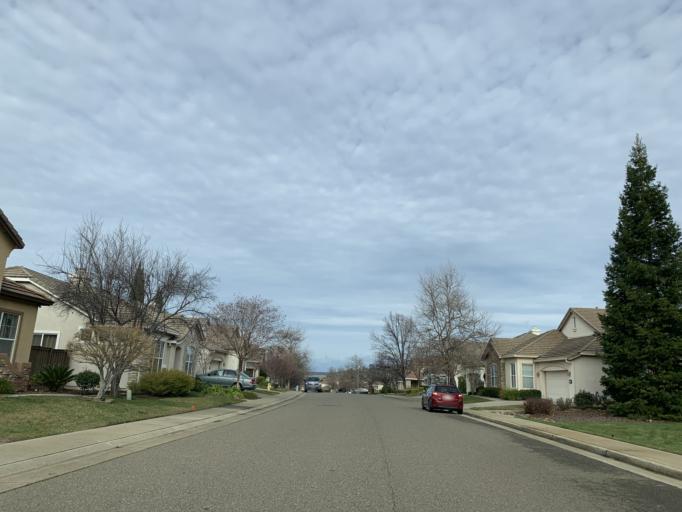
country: US
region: California
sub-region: El Dorado County
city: El Dorado Hills
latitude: 38.6811
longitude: -121.1020
